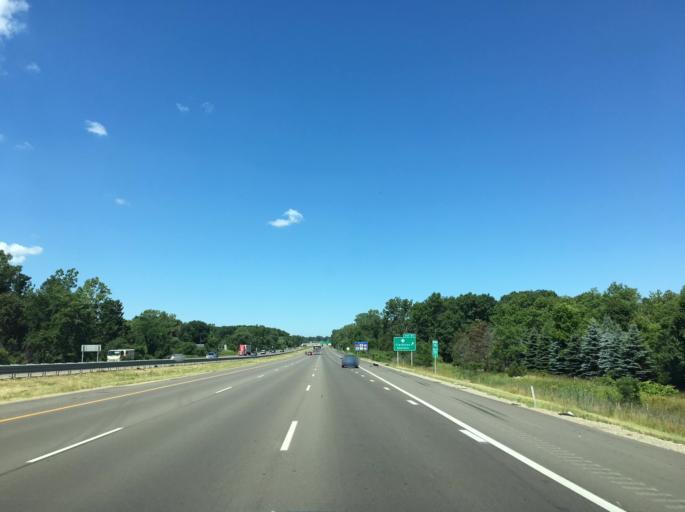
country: US
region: Michigan
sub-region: Oakland County
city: Clarkston
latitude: 42.7458
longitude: -83.4026
